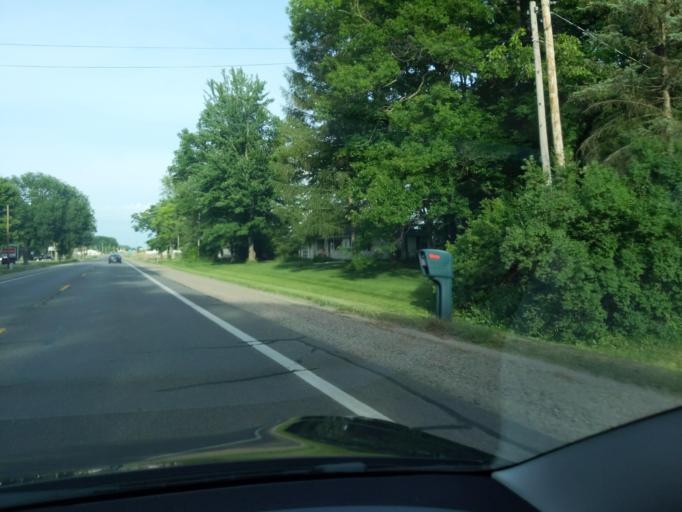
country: US
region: Michigan
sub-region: Montcalm County
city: Lakeview
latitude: 43.4315
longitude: -85.2720
